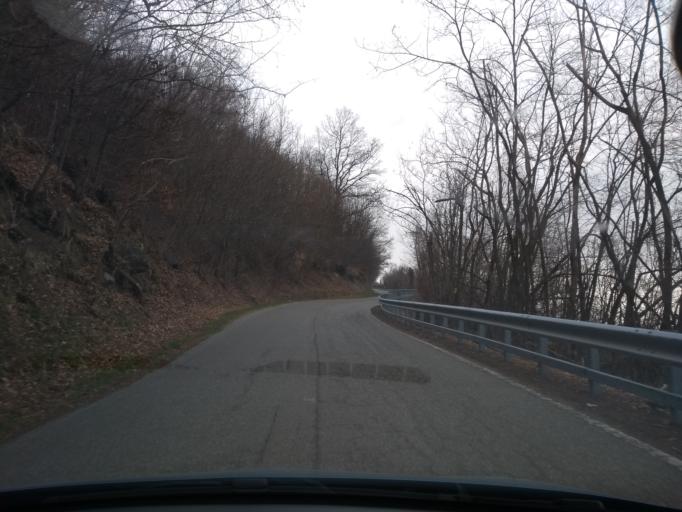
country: IT
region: Piedmont
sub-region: Provincia di Torino
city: Palazzo Canavese
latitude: 45.4715
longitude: 7.9783
